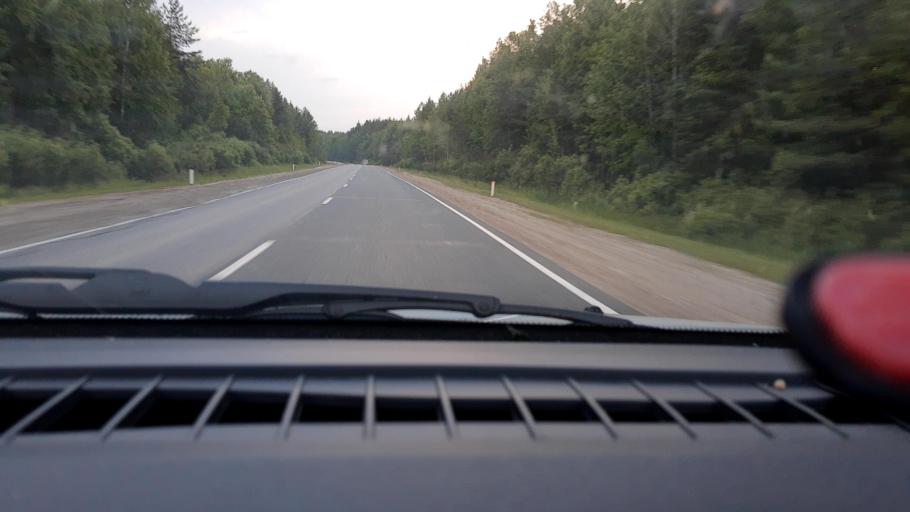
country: RU
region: Nizjnij Novgorod
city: Arzamas
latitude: 55.4167
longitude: 43.9132
